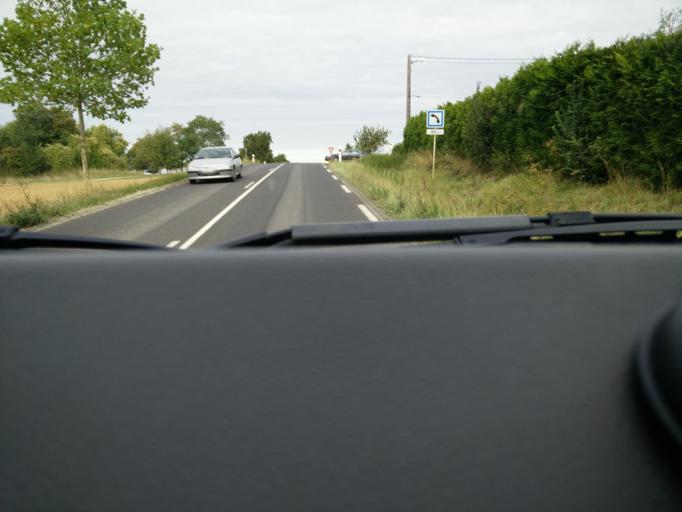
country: FR
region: Lorraine
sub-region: Departement de Meurthe-et-Moselle
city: Montauville
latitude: 48.9011
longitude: 5.9590
